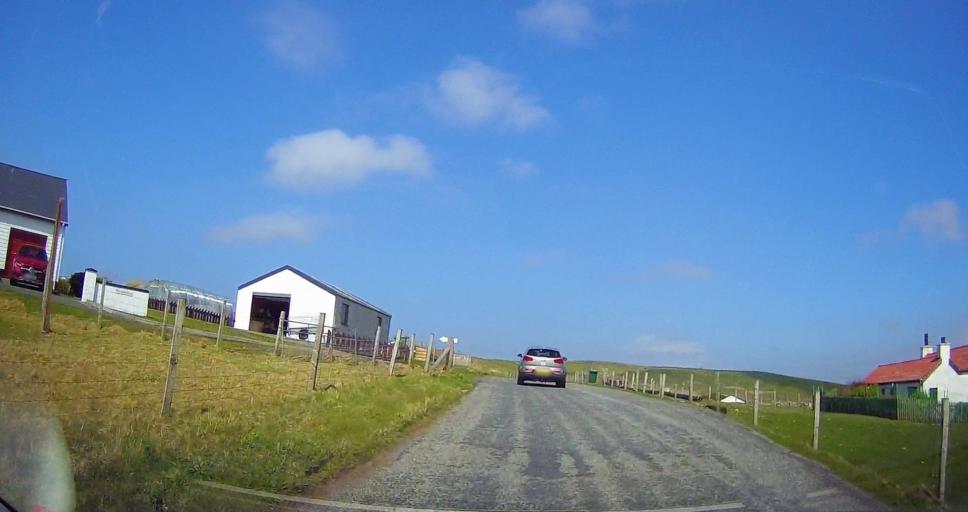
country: GB
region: Scotland
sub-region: Shetland Islands
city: Sandwick
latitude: 60.0686
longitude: -1.3396
